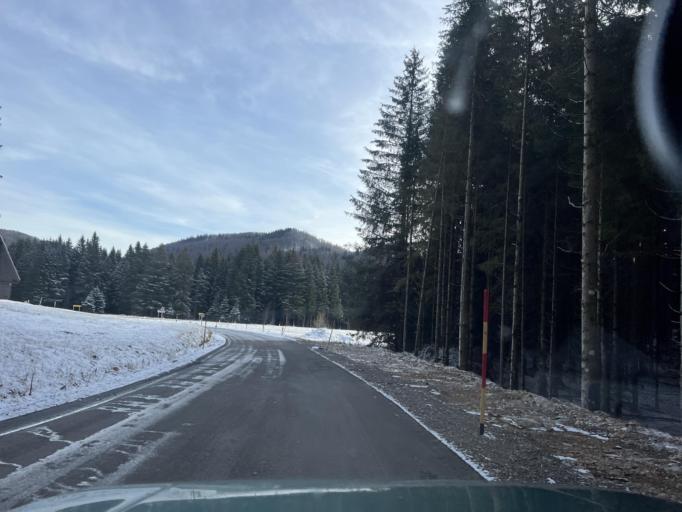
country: SI
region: Nova Gorica
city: Sempas
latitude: 45.9819
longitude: 13.8249
